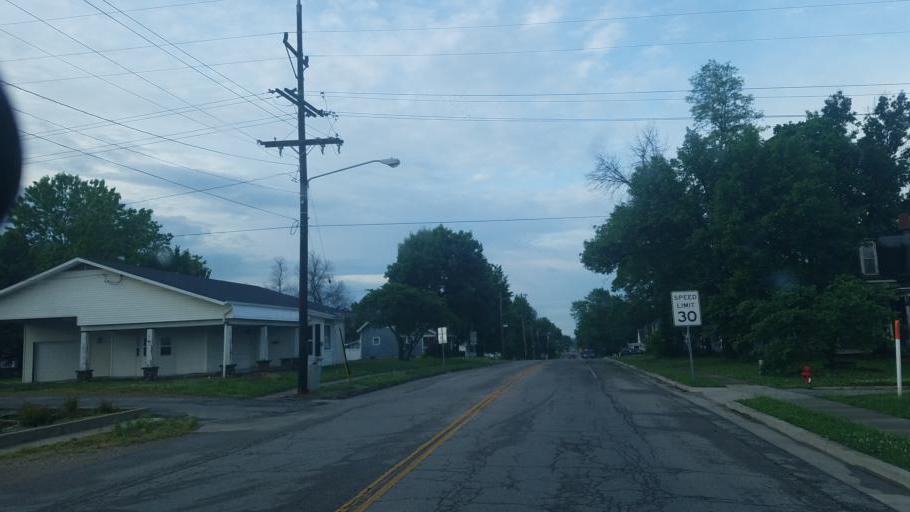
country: US
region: Missouri
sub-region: Moniteau County
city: California
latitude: 38.6271
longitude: -92.5666
